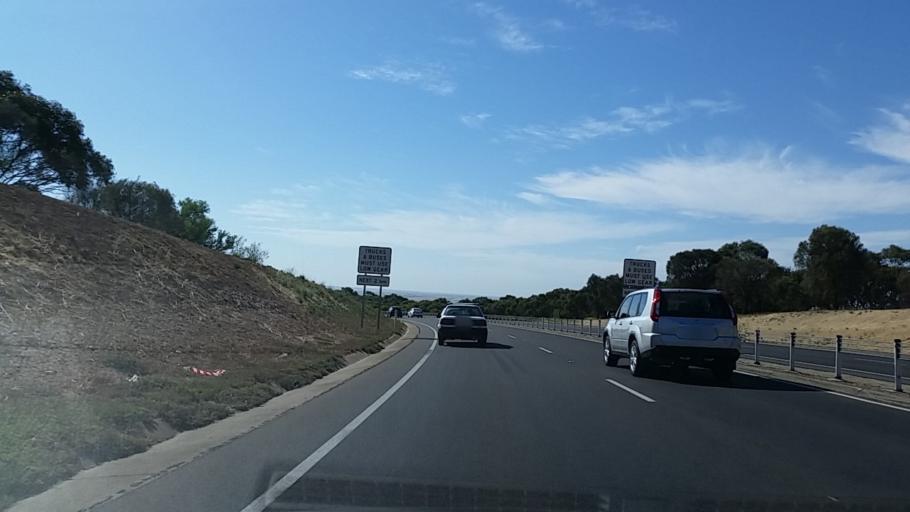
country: AU
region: South Australia
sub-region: Tea Tree Gully
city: Golden Grove
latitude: -34.7840
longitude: 138.6929
